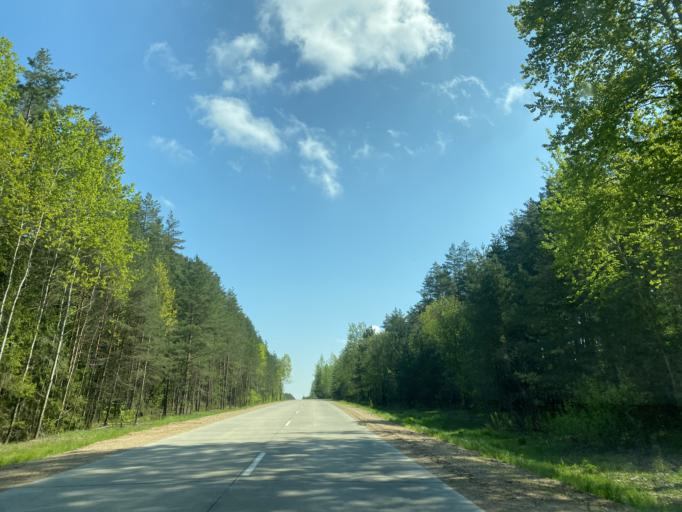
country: BY
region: Minsk
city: Horad Barysaw
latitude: 54.1623
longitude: 28.4951
